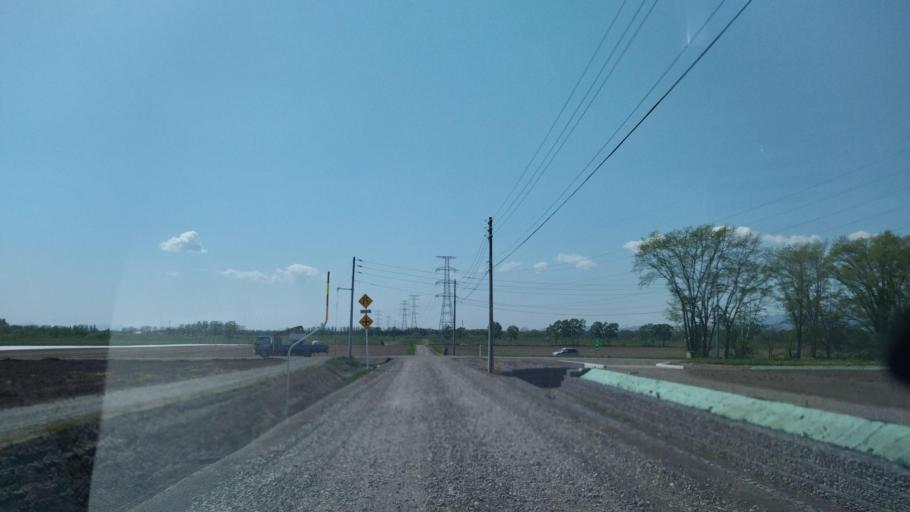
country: JP
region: Hokkaido
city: Otofuke
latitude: 43.1419
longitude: 143.2221
